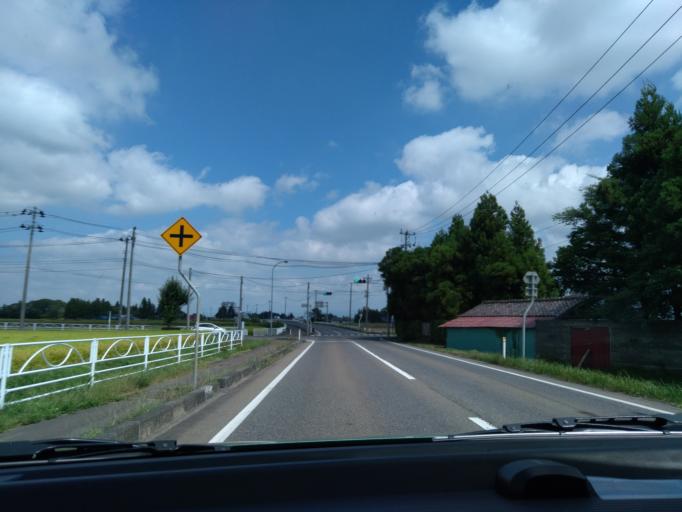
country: JP
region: Iwate
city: Hanamaki
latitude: 39.4002
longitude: 141.0649
